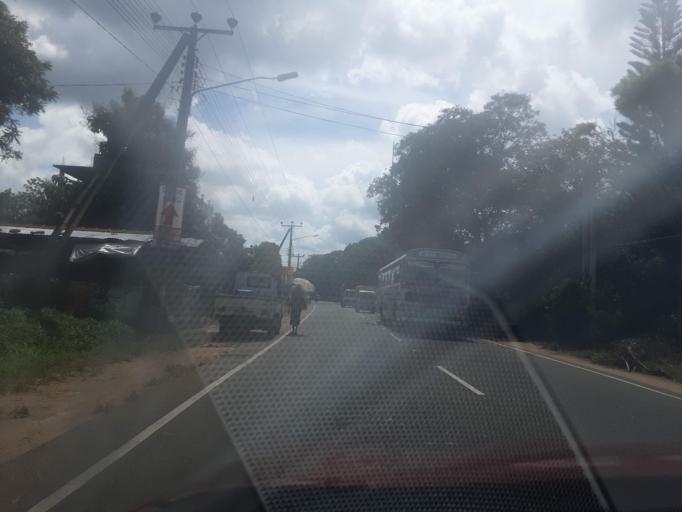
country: LK
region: North Western
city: Kuliyapitiya
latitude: 7.4700
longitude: 80.0482
